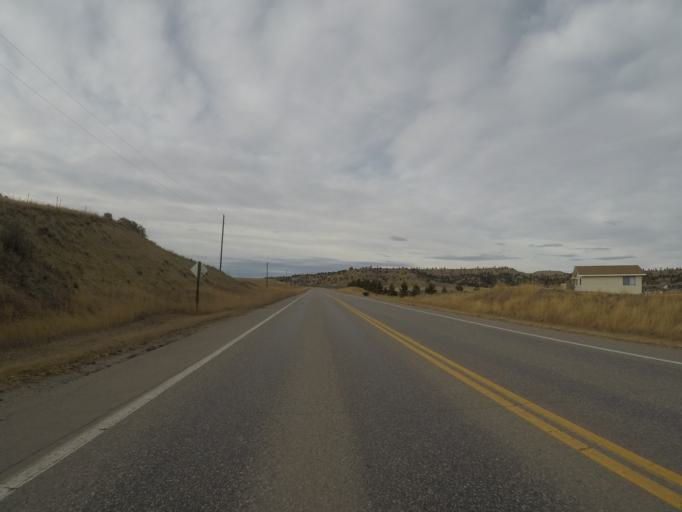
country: US
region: Montana
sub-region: Yellowstone County
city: Laurel
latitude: 45.8123
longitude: -108.6775
